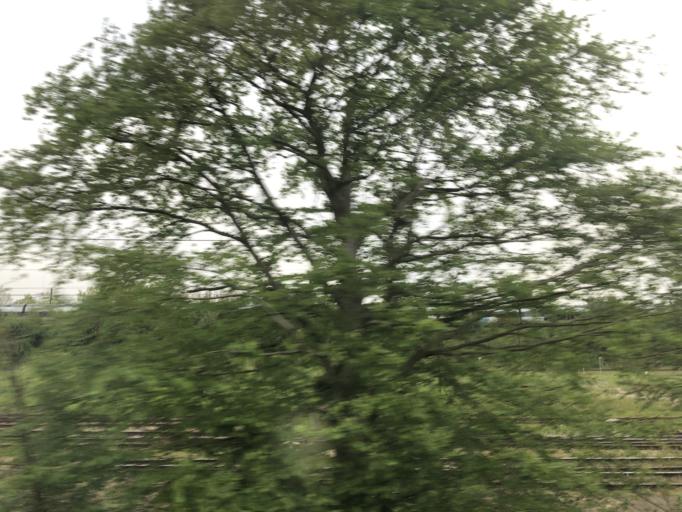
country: DK
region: South Denmark
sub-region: Fredericia Kommune
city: Fredericia
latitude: 55.5792
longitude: 9.7350
